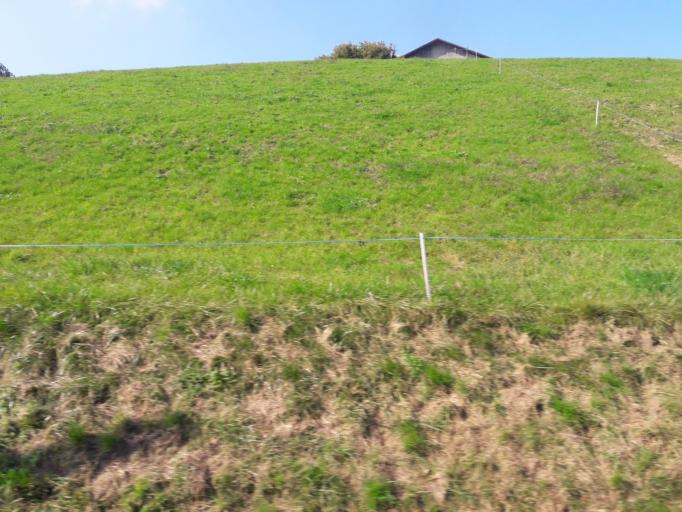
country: CH
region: Lucerne
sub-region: Lucerne-Land District
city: Udligenswil
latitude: 47.0715
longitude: 8.4192
